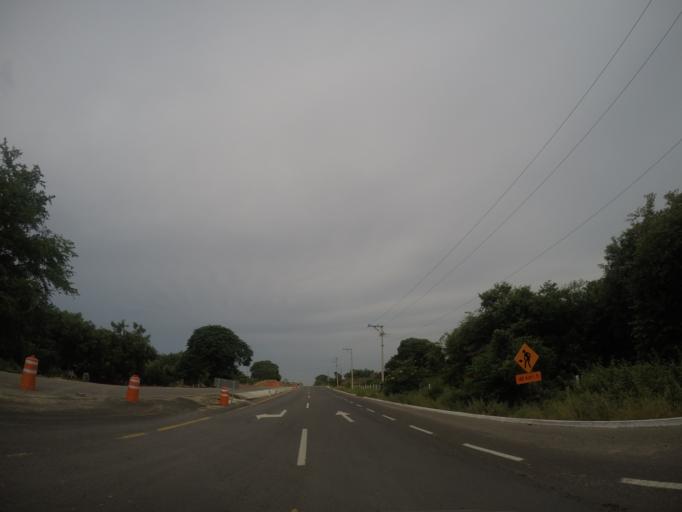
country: MX
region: Oaxaca
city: Santa Maria Tonameca
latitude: 15.7232
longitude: -96.6192
